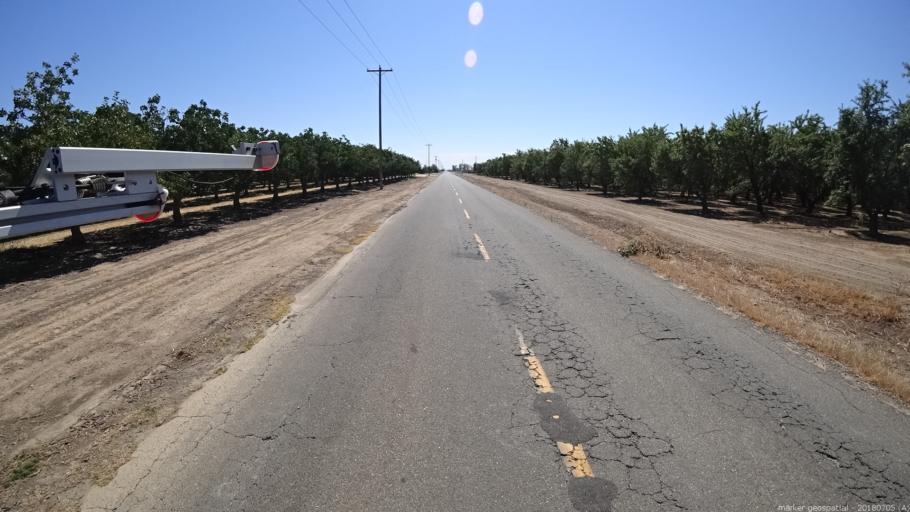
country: US
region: California
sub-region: Madera County
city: Fairmead
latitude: 37.0981
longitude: -120.1403
